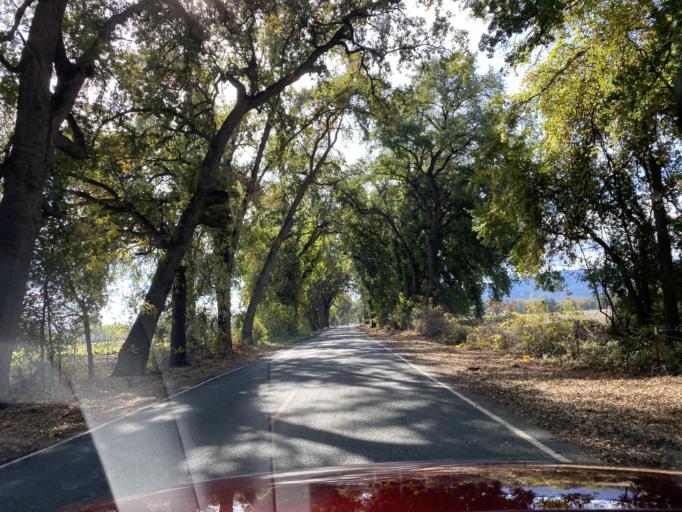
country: US
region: California
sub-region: Colusa County
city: Maxwell
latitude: 39.3919
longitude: -122.5519
